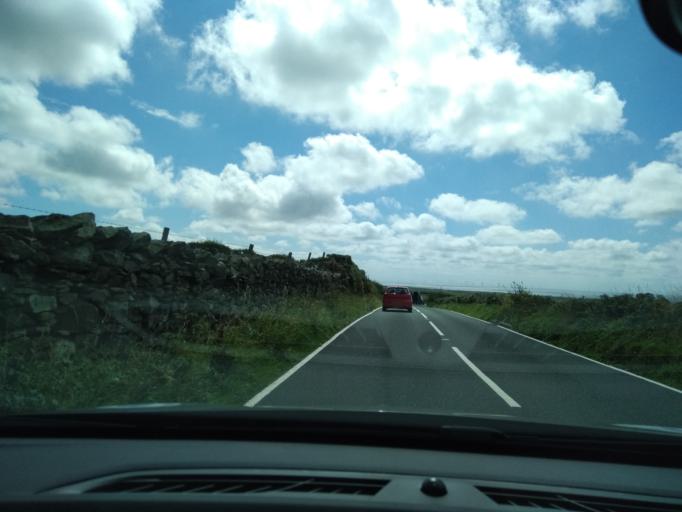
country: GB
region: England
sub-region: Cumbria
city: Millom
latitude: 54.2377
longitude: -3.3218
